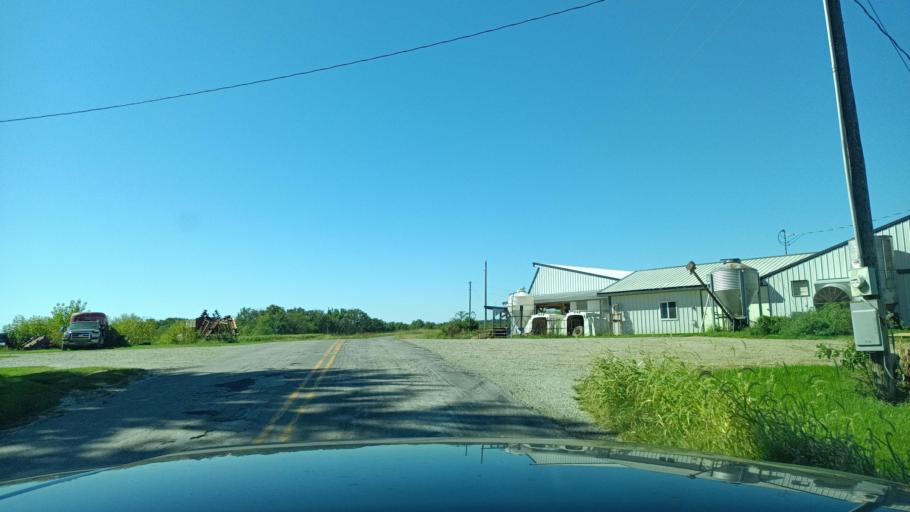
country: US
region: Missouri
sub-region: Scotland County
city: Memphis
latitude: 40.3537
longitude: -92.2371
